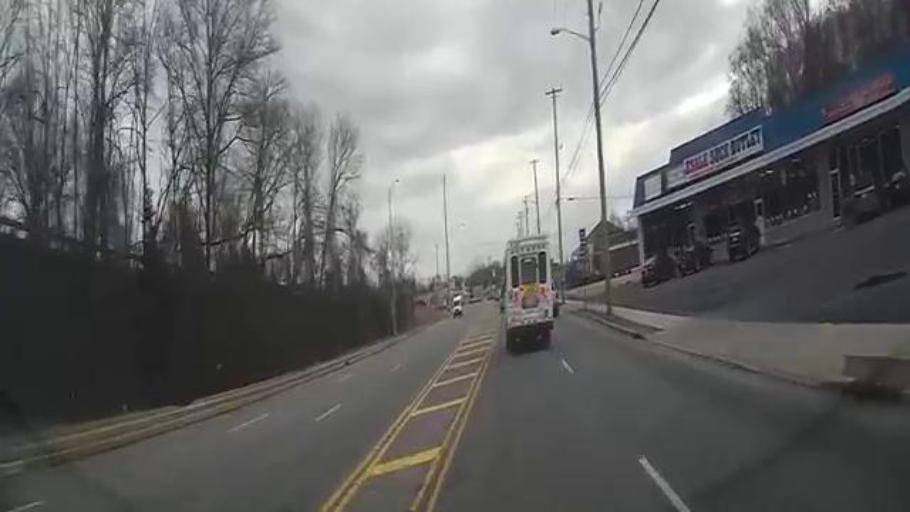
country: US
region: New Jersey
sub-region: Camden County
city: Berlin
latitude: 39.7988
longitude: -74.9350
